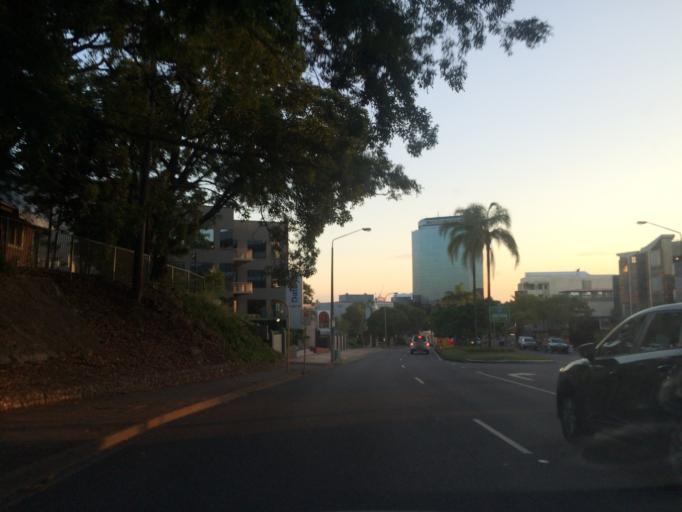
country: AU
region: Queensland
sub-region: Brisbane
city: Toowong
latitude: -27.4877
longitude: 152.9904
